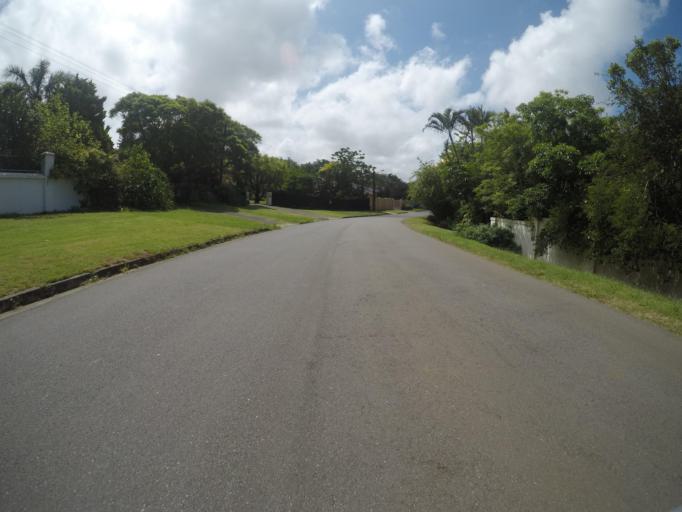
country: ZA
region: Eastern Cape
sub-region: Buffalo City Metropolitan Municipality
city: East London
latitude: -32.9743
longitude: 27.9064
